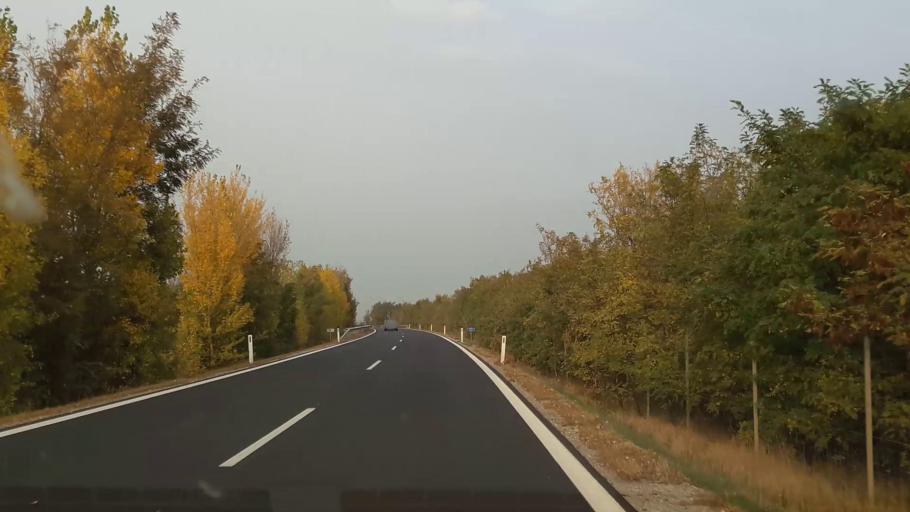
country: AT
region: Burgenland
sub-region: Politischer Bezirk Neusiedl am See
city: Gols
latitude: 47.9296
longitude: 16.9133
